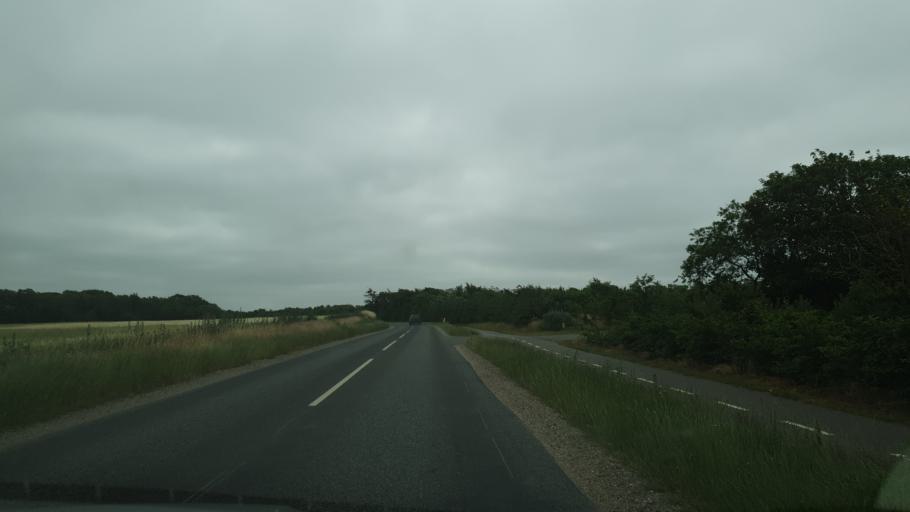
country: DK
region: Central Jutland
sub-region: Ringkobing-Skjern Kommune
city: Ringkobing
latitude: 55.9862
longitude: 8.3392
